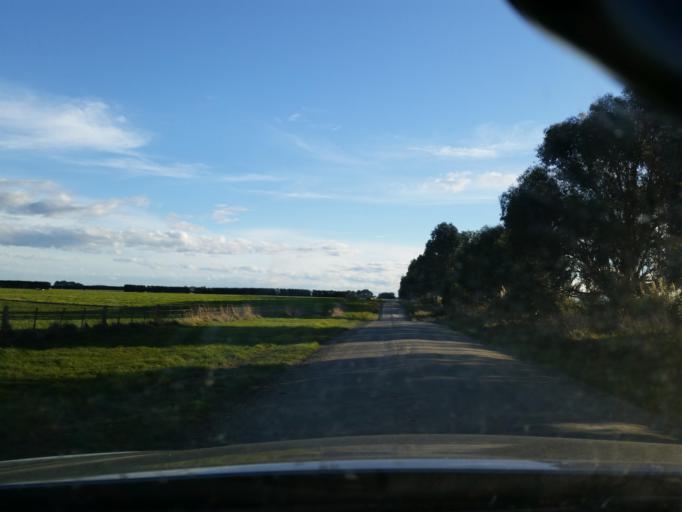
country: NZ
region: Southland
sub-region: Gore District
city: Gore
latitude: -46.3580
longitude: 168.7018
